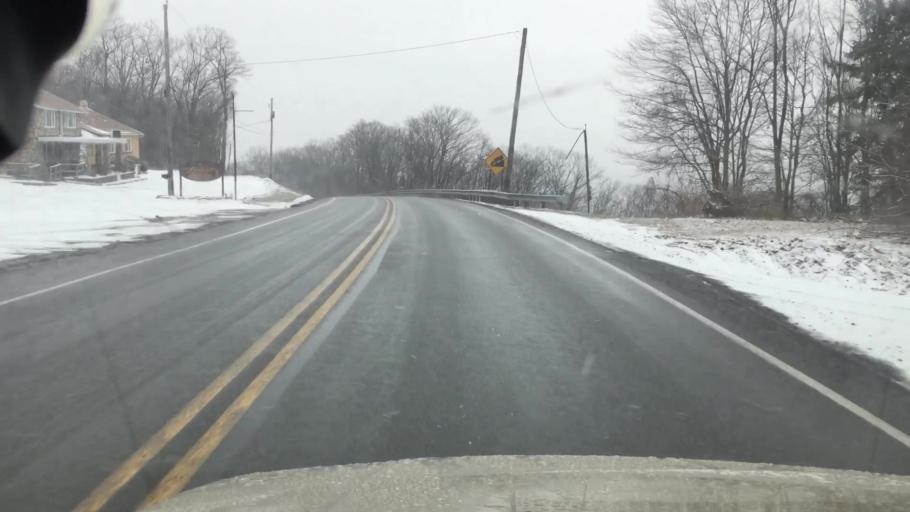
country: US
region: Pennsylvania
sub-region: Luzerne County
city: Conyngham
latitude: 41.0308
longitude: -76.1008
